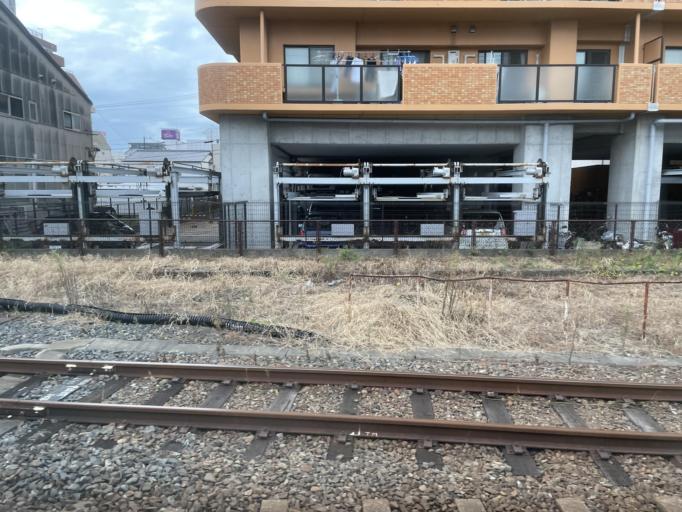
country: JP
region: Wakayama
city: Wakayama-shi
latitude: 34.2359
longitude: 135.1905
